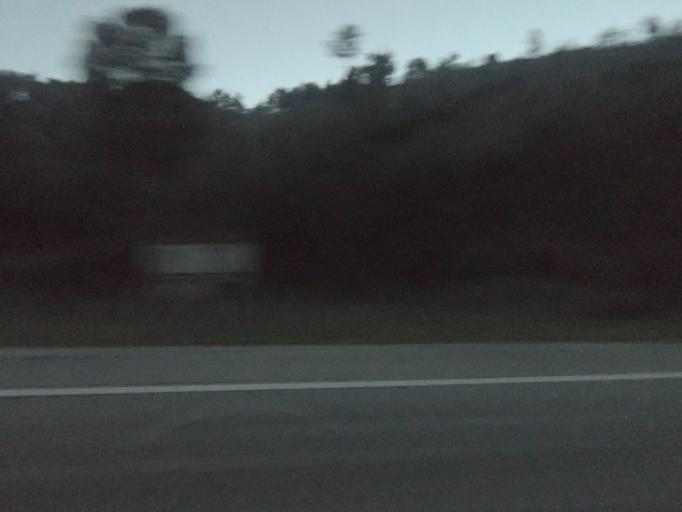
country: PT
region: Porto
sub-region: Baiao
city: Baiao
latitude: 41.2328
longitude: -8.0147
